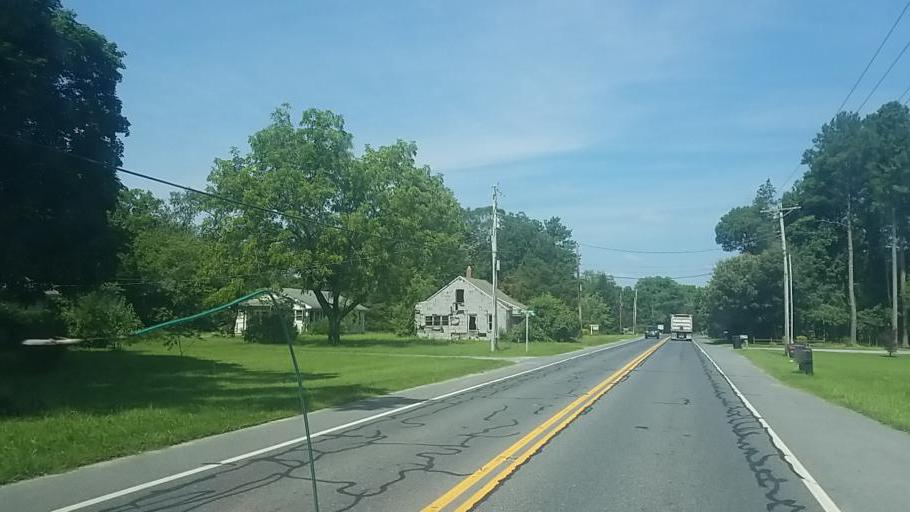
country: US
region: Delaware
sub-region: Sussex County
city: Seaford
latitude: 38.6673
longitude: -75.5686
